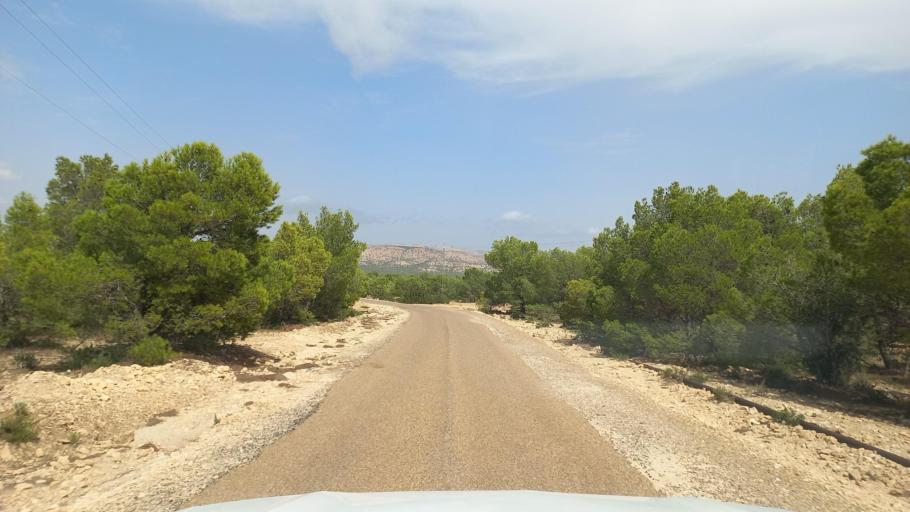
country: TN
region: Al Qasrayn
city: Sbiba
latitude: 35.3965
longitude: 8.9135
